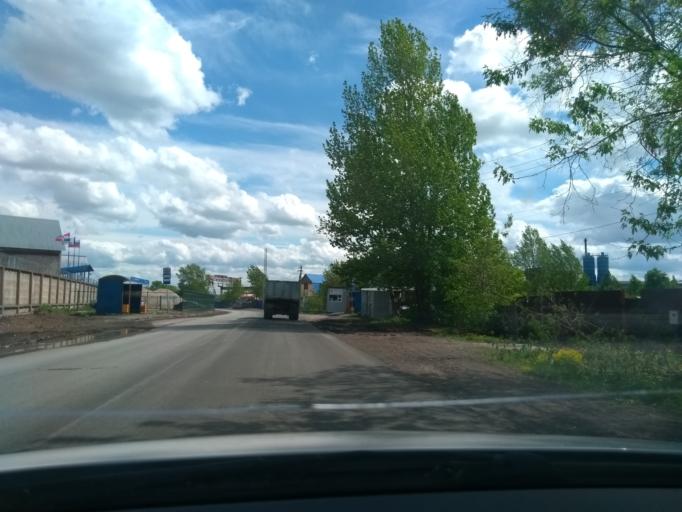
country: RU
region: Perm
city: Kondratovo
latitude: 58.0117
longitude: 56.0635
